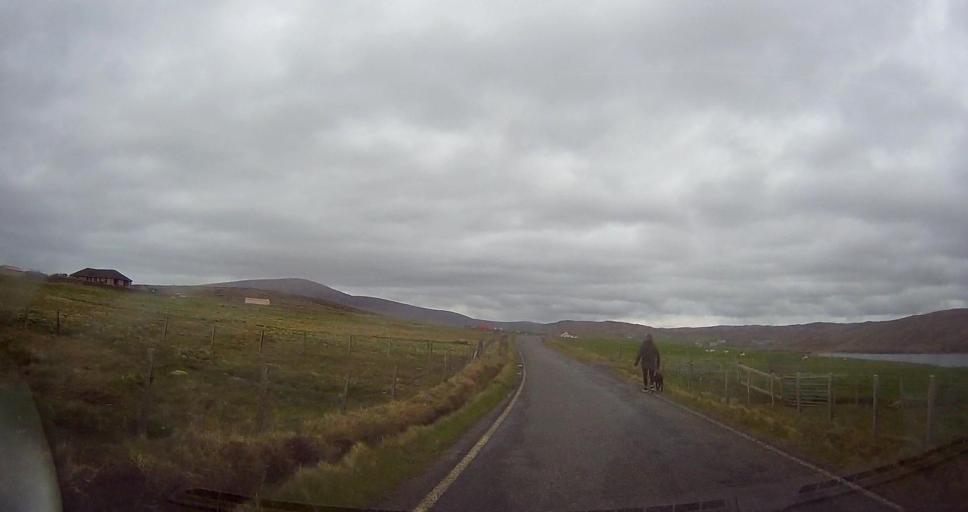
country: GB
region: Scotland
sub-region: Shetland Islands
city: Lerwick
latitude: 60.4799
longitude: -1.4796
